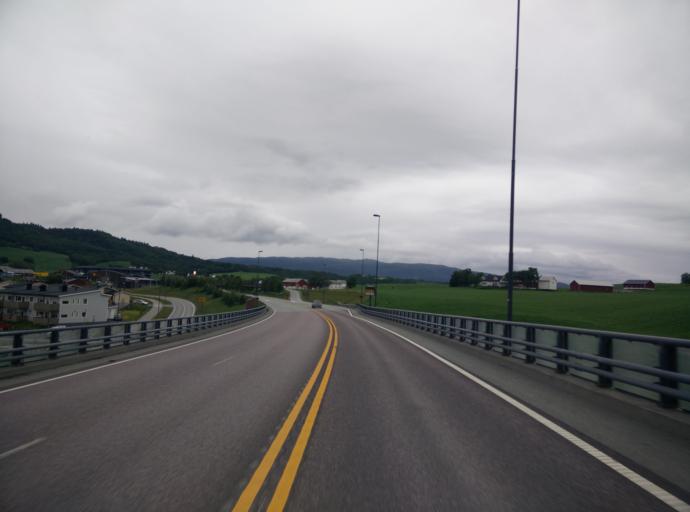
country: NO
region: Sor-Trondelag
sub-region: Skaun
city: Borsa
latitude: 63.3083
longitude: 10.1660
